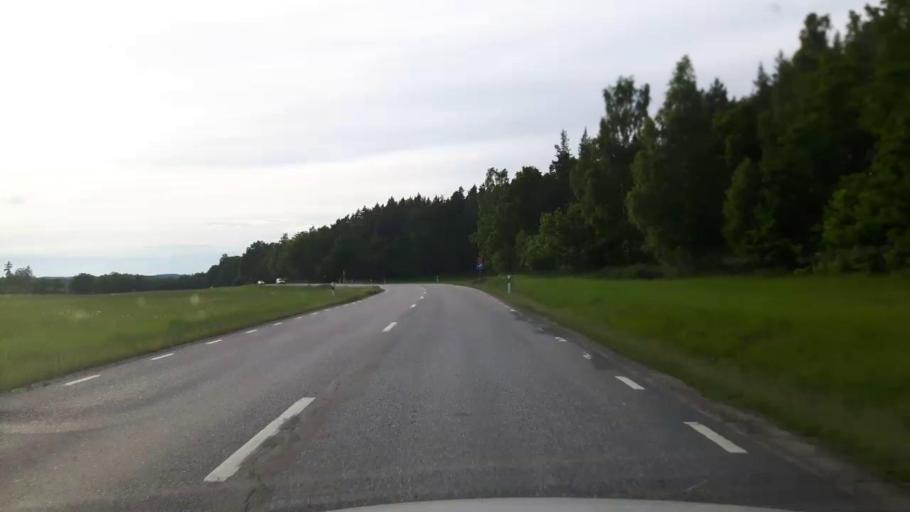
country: SE
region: Uppsala
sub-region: Habo Kommun
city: Balsta
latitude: 59.6493
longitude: 17.4242
